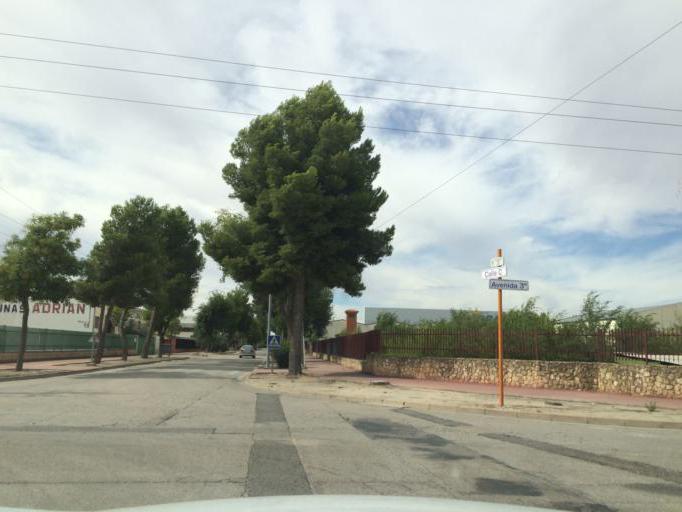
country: ES
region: Castille-La Mancha
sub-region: Provincia de Albacete
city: Albacete
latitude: 39.0134
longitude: -1.8803
